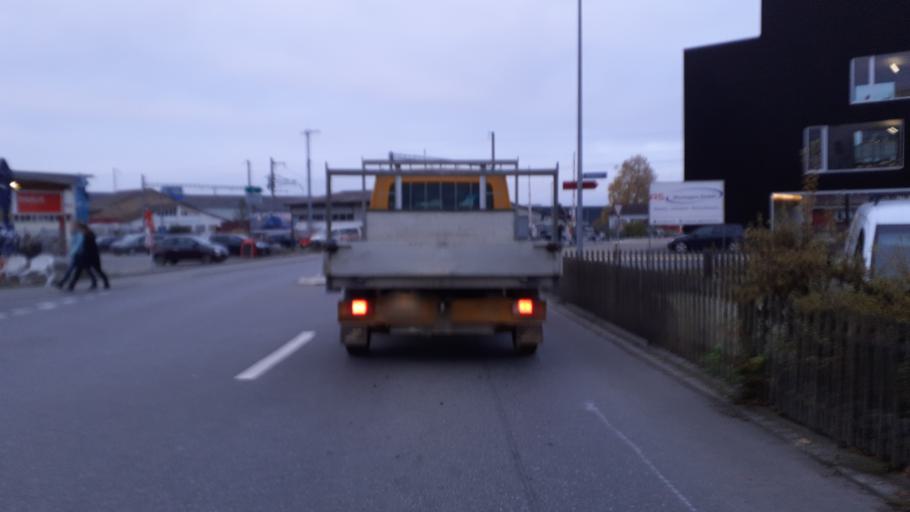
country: CH
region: Saint Gallen
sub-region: Wahlkreis Rheintal
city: Altstatten
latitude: 47.3756
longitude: 9.5566
